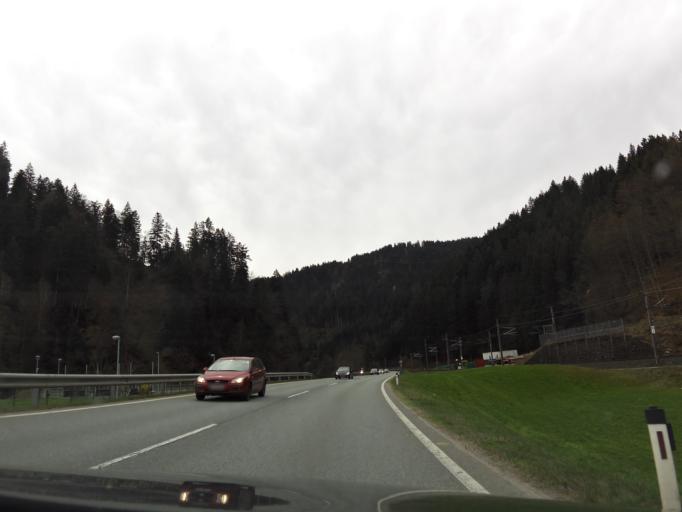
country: AT
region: Tyrol
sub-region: Politischer Bezirk Kitzbuhel
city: Itter
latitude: 47.4728
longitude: 12.1352
